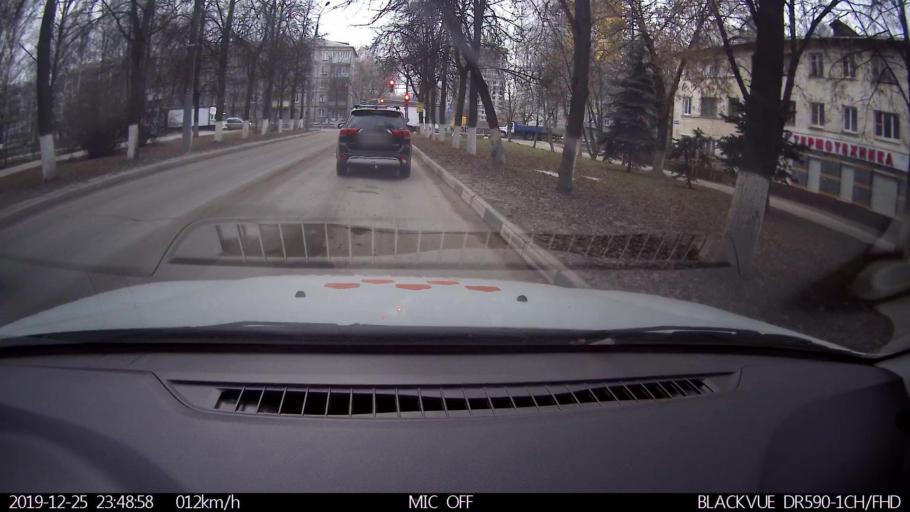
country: RU
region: Nizjnij Novgorod
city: Gorbatovka
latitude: 56.3394
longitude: 43.8460
